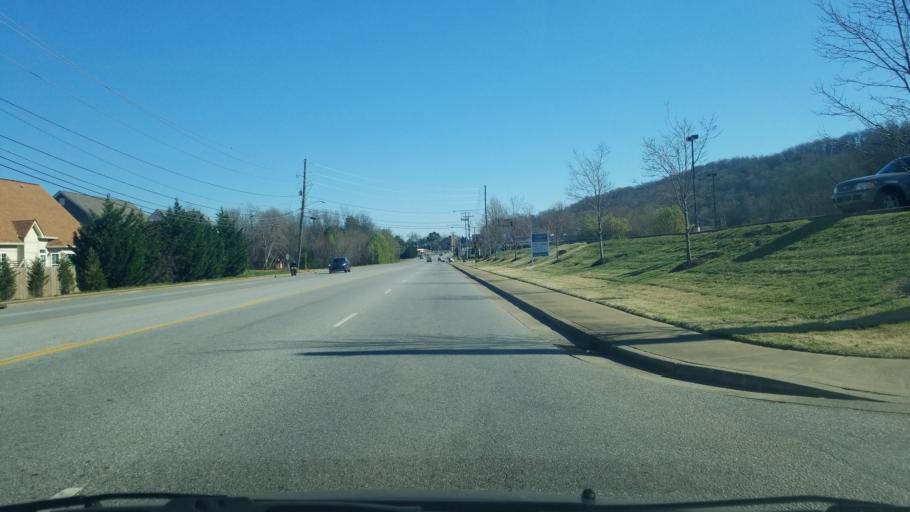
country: US
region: Tennessee
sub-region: Hamilton County
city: Middle Valley
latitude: 35.1518
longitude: -85.2011
